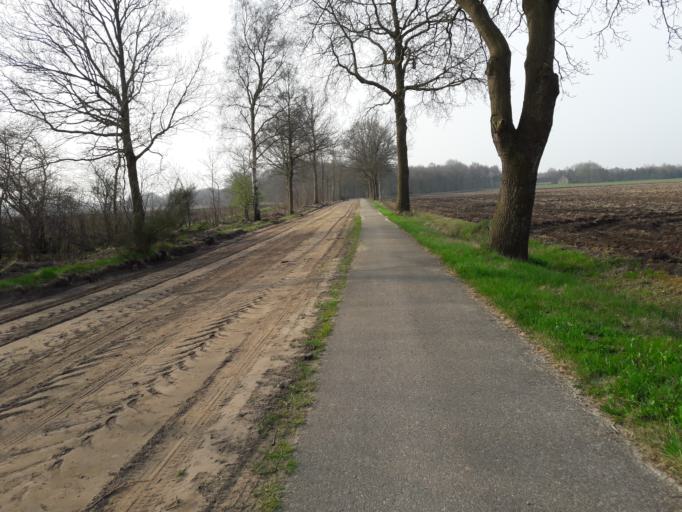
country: NL
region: Drenthe
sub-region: Gemeente Aa en Hunze
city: Anloo
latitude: 52.9490
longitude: 6.6636
